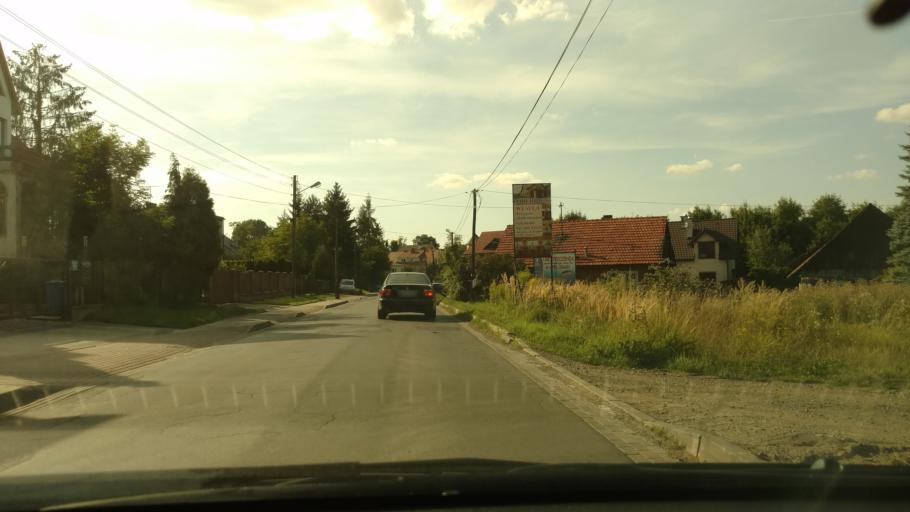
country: PL
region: Lesser Poland Voivodeship
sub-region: Powiat krakowski
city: Michalowice
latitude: 50.1156
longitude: 19.9718
